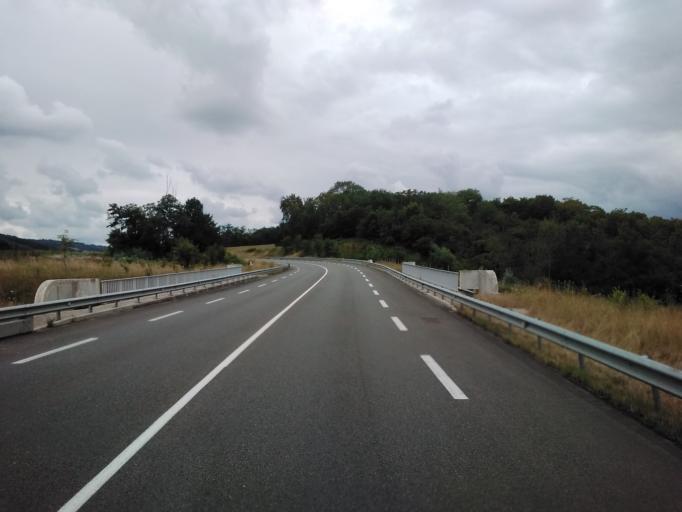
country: FR
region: Franche-Comte
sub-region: Departement du Jura
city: Montmorot
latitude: 46.6573
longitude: 5.5079
